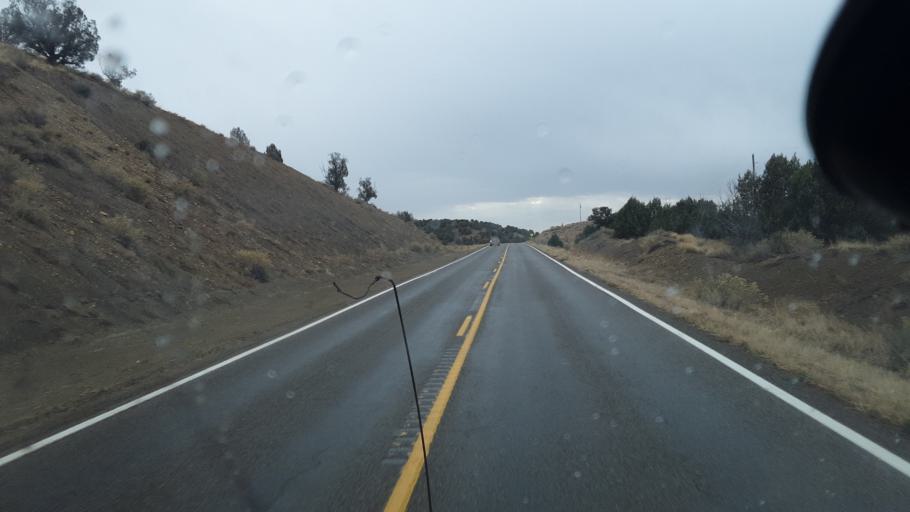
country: US
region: New Mexico
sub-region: San Juan County
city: Spencerville
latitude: 37.0258
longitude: -108.1822
